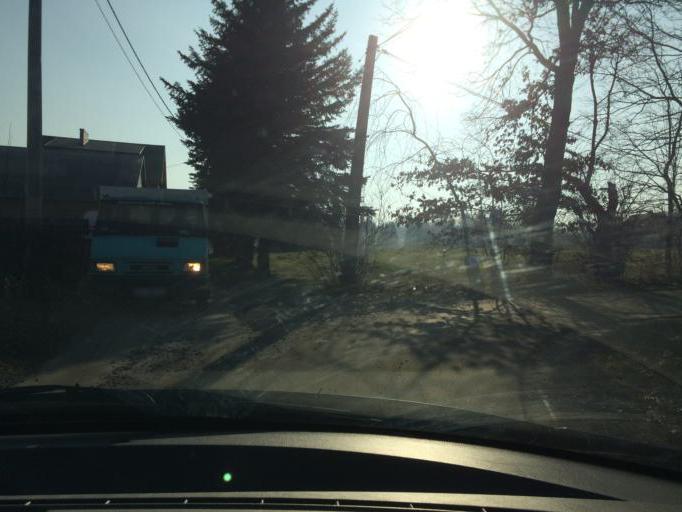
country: PL
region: Lesser Poland Voivodeship
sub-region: Powiat wielicki
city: Czarnochowice
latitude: 50.0049
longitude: 20.0420
